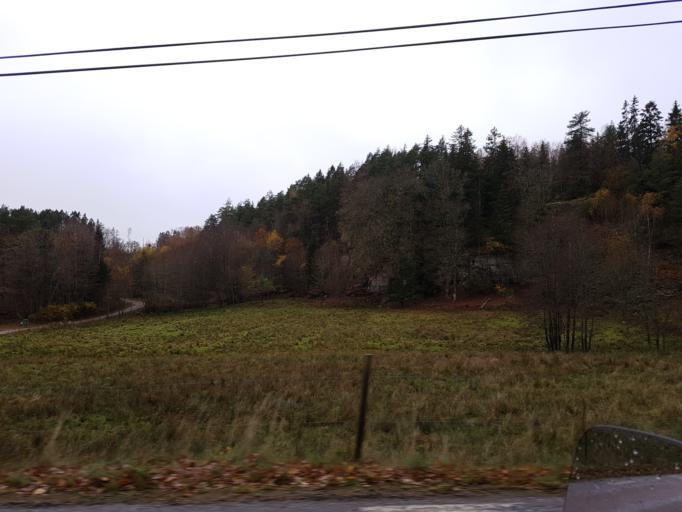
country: SE
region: Vaestra Goetaland
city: Svanesund
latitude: 58.1941
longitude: 11.8277
